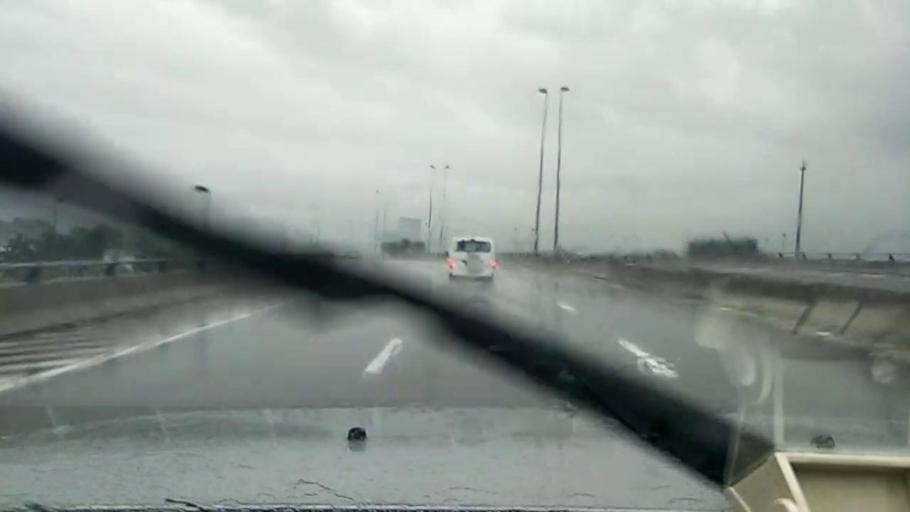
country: MY
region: Selangor
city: Kampong Baharu Balakong
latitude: 2.9920
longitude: 101.7728
